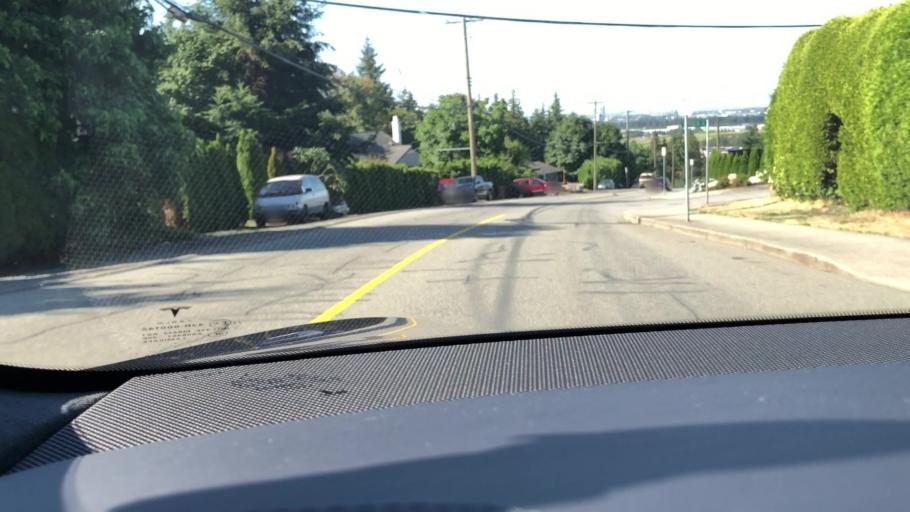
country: CA
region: British Columbia
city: Burnaby
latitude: 49.2087
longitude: -122.9732
